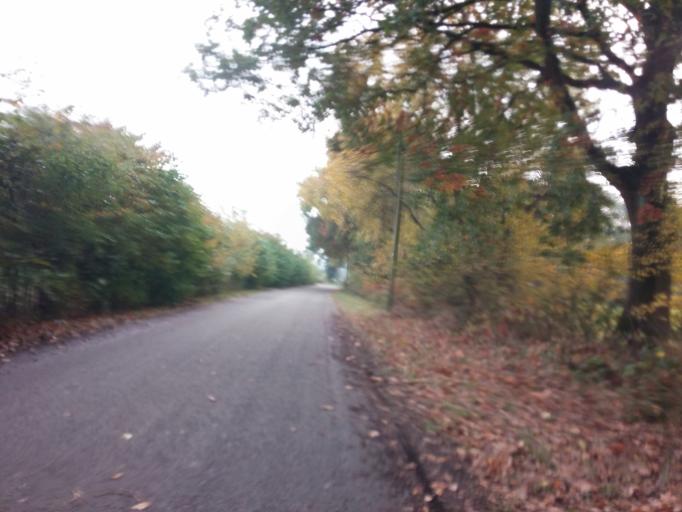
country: DE
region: North Rhine-Westphalia
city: Dorsten
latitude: 51.6336
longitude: 6.9811
